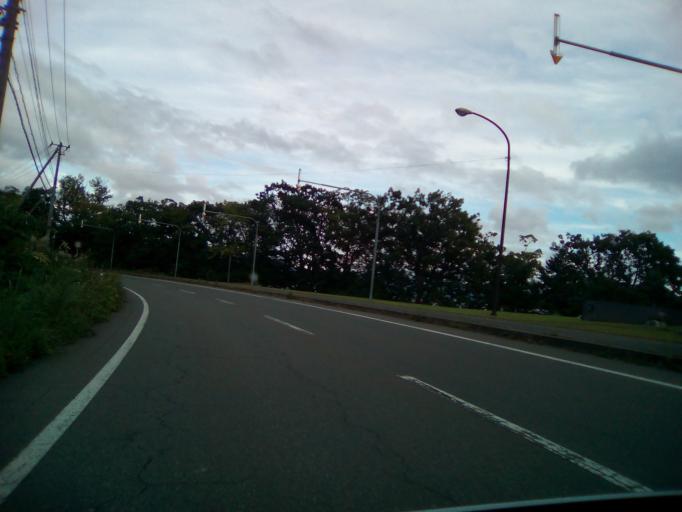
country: JP
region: Hokkaido
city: Date
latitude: 42.6462
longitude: 140.8395
